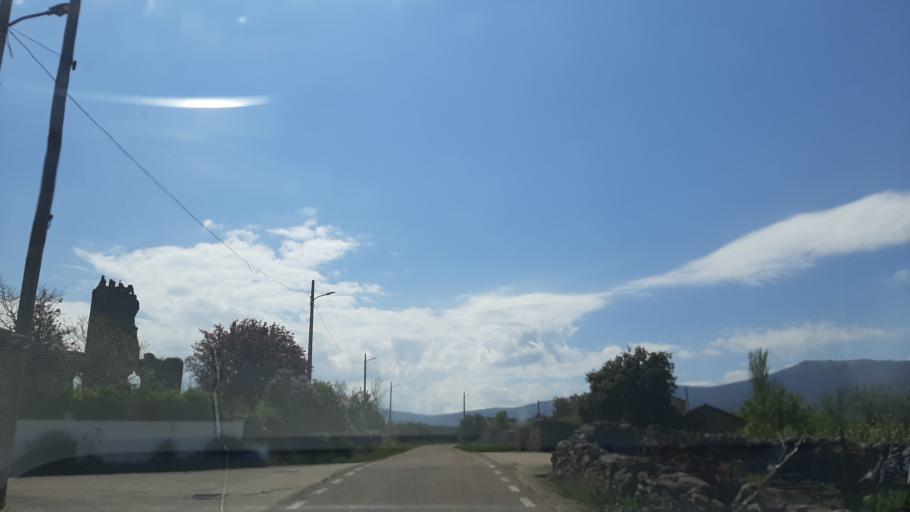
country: ES
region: Castille and Leon
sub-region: Provincia de Salamanca
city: Tejeda y Segoyuela
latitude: 40.6317
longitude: -6.0222
